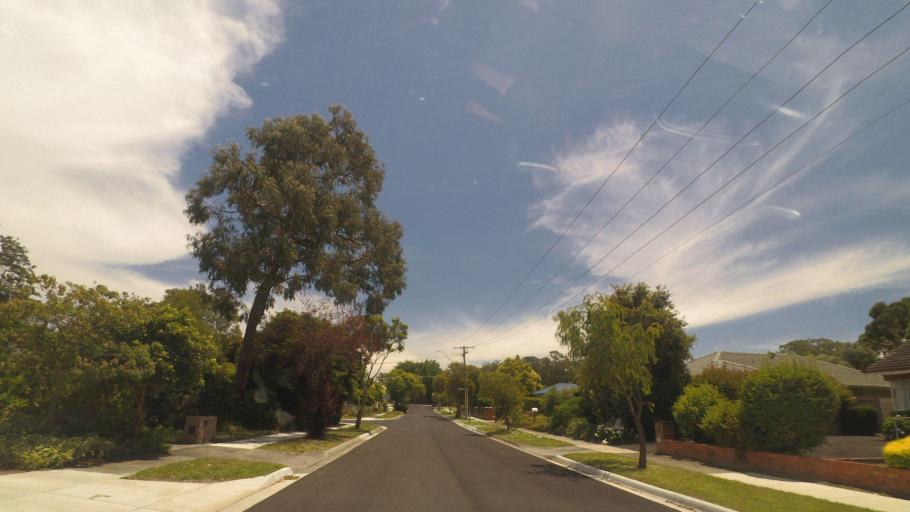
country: AU
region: Victoria
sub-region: Knox
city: Boronia
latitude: -37.8554
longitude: 145.2940
